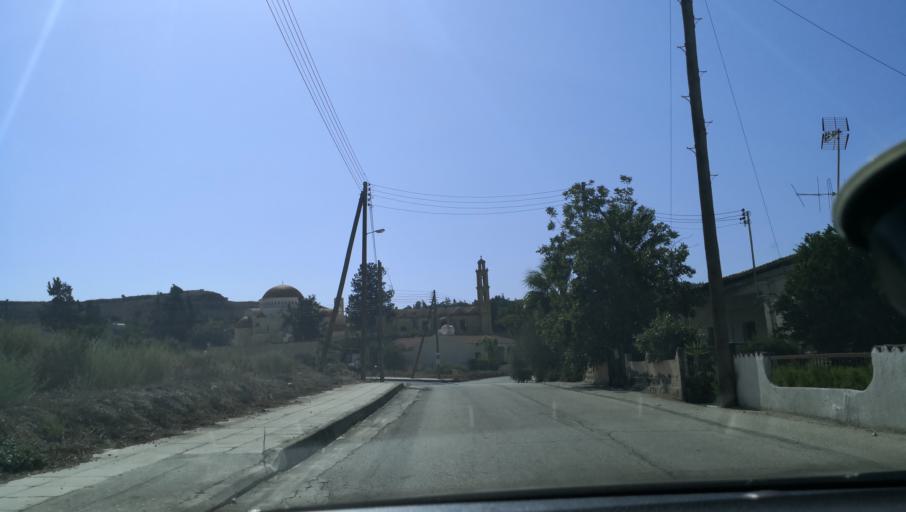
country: CY
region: Lefkosia
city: Mammari
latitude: 35.1748
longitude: 33.2069
